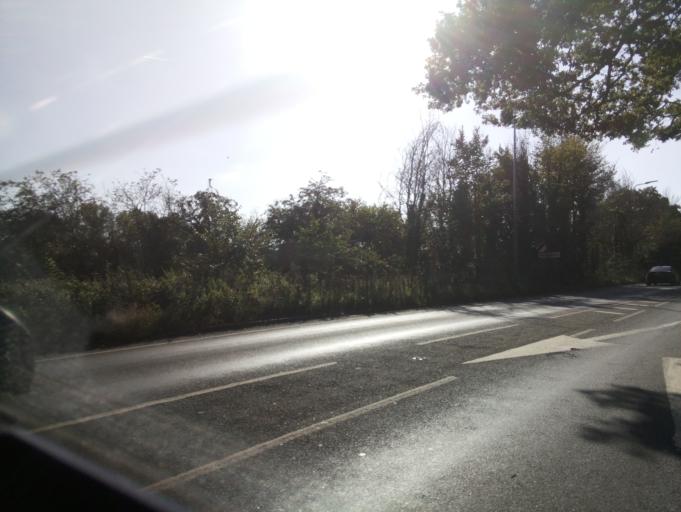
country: GB
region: England
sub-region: Hampshire
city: Tadley
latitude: 51.3975
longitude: -1.1819
